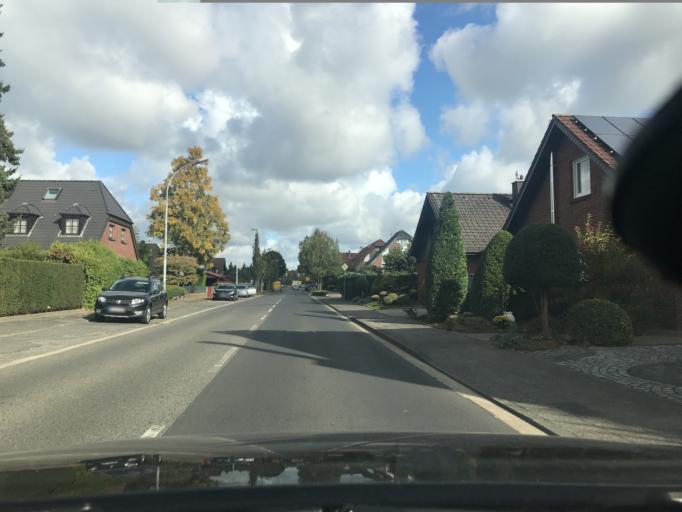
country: DE
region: North Rhine-Westphalia
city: Tonisvorst
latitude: 51.3273
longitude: 6.4938
